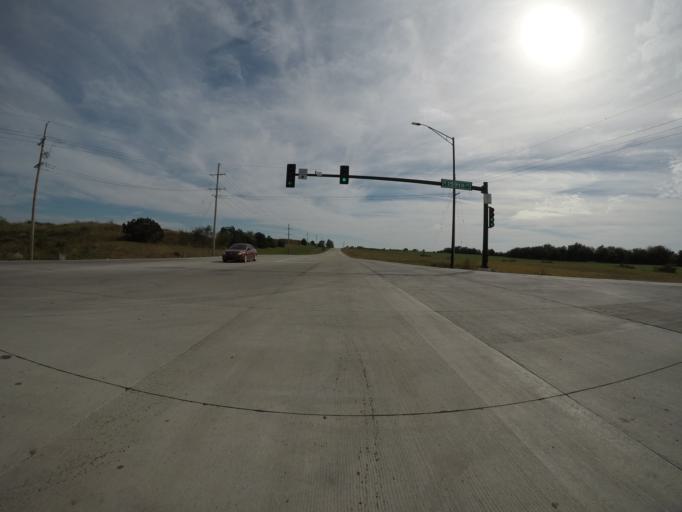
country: US
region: Kansas
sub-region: Johnson County
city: Gardner
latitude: 38.8401
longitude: -94.8713
